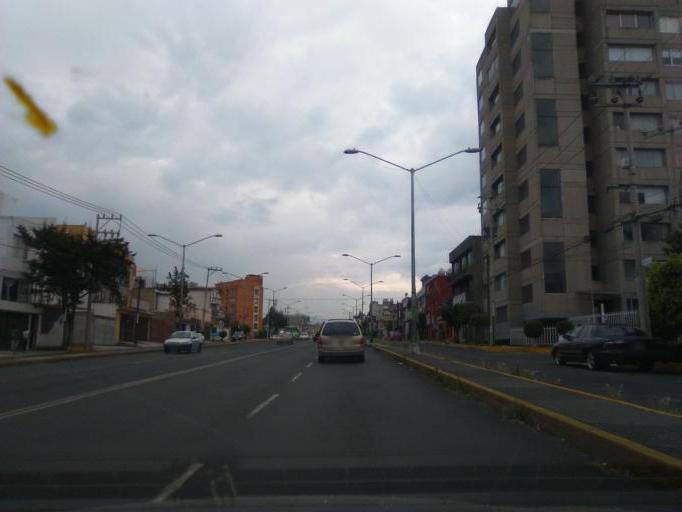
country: MX
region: Mexico City
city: Alvaro Obregon
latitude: 19.3687
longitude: -99.2253
